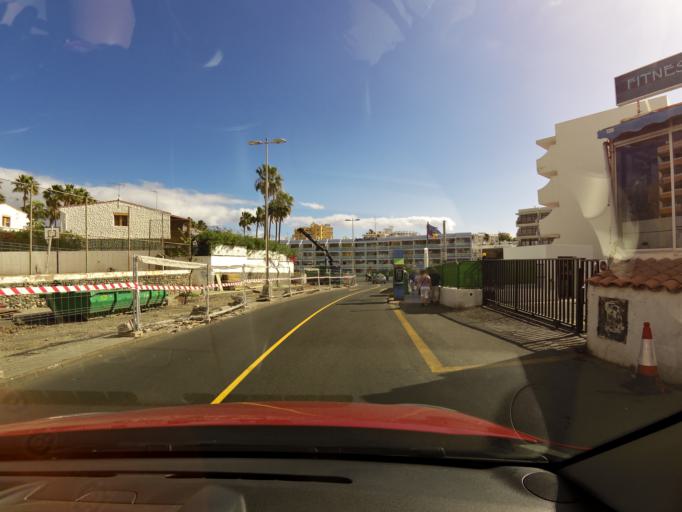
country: ES
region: Canary Islands
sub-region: Provincia de Las Palmas
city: Playa del Ingles
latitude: 27.7589
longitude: -15.5739
